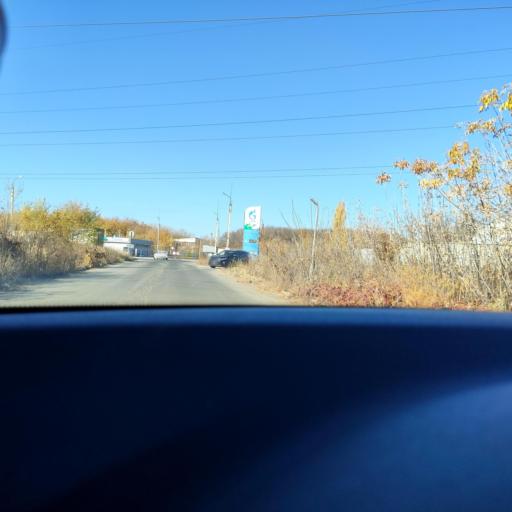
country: RU
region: Samara
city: Petra-Dubrava
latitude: 53.2593
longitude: 50.2862
